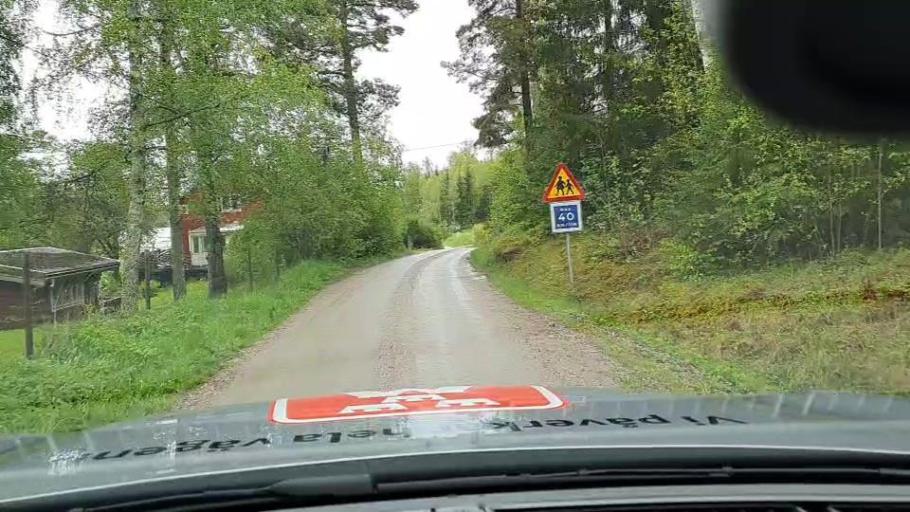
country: SE
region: Soedermanland
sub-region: Nykopings Kommun
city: Svalsta
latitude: 58.6454
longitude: 16.9319
